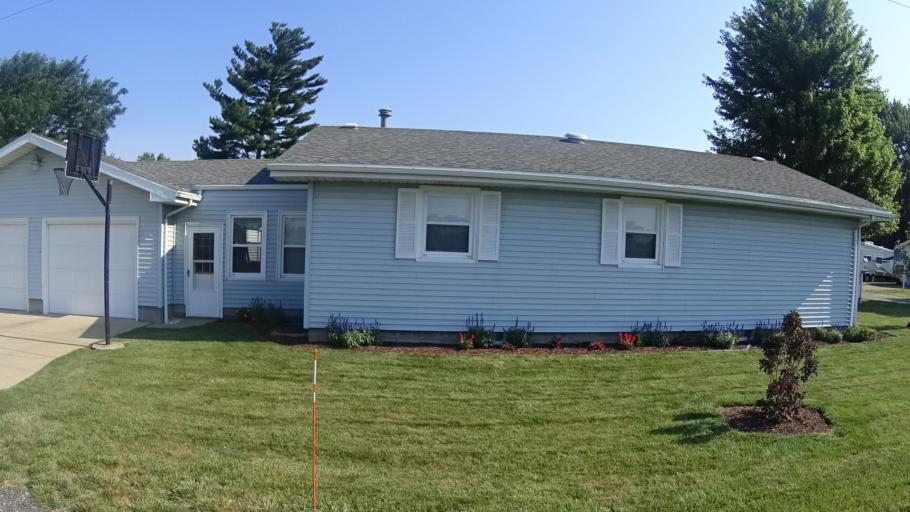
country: US
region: Ohio
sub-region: Erie County
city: Huron
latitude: 41.4064
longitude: -82.5825
